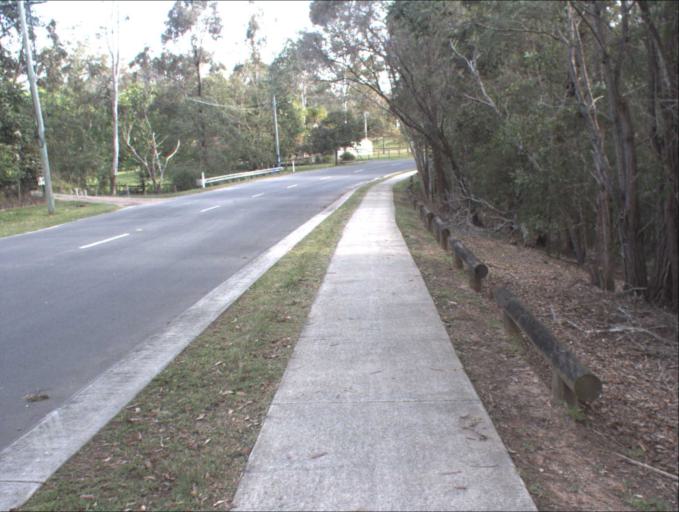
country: AU
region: Queensland
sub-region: Brisbane
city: Forest Lake
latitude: -27.6633
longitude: 152.9983
